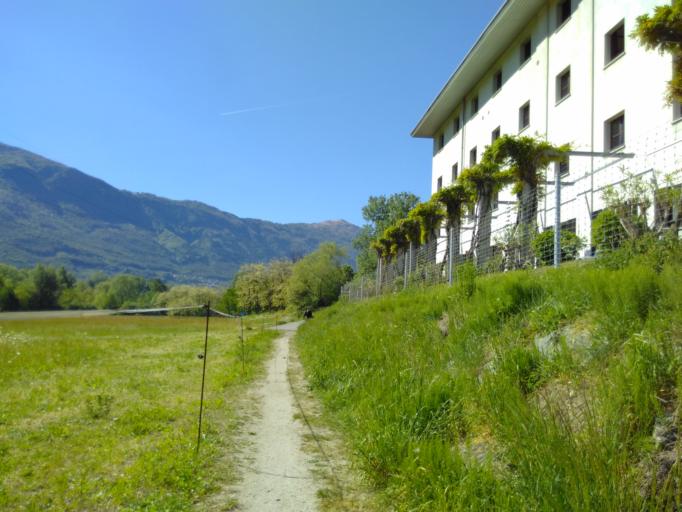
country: CH
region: Ticino
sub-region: Bellinzona District
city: Monte Carasso
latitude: 46.1837
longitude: 9.0036
